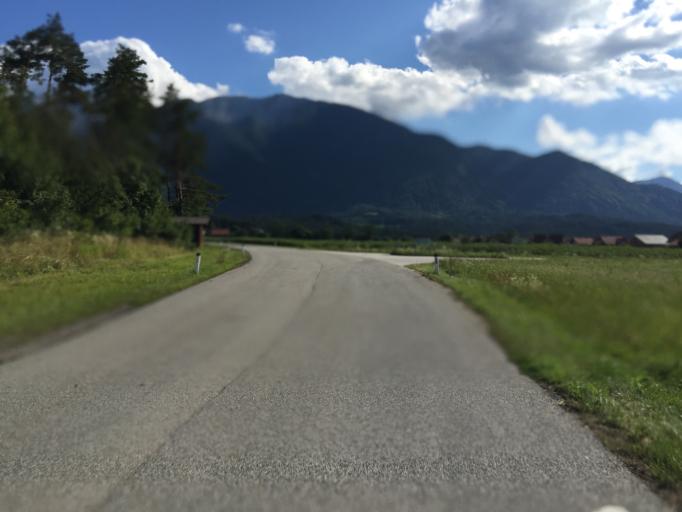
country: AT
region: Carinthia
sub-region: Politischer Bezirk Volkermarkt
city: Feistritz ob Bleiburg
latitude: 46.5650
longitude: 14.7676
